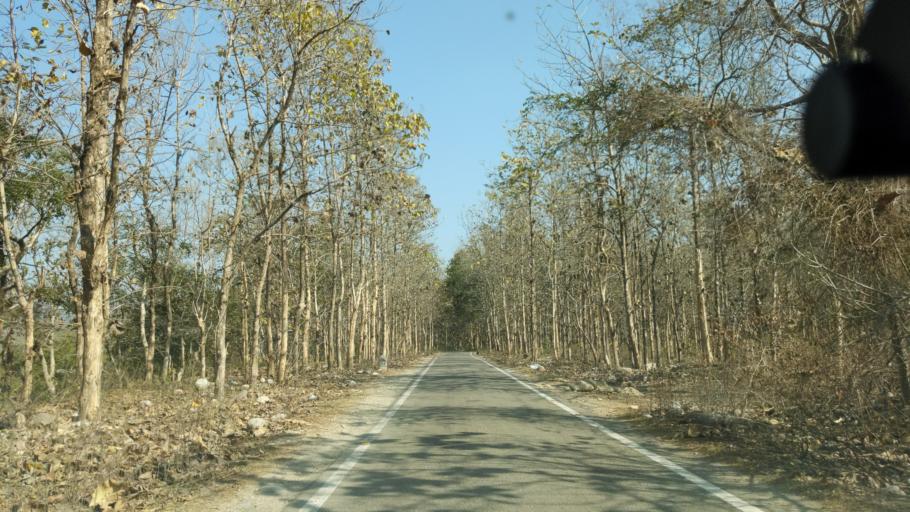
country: IN
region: Uttarakhand
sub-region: Naini Tal
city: Ramnagar
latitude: 29.4237
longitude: 79.1389
